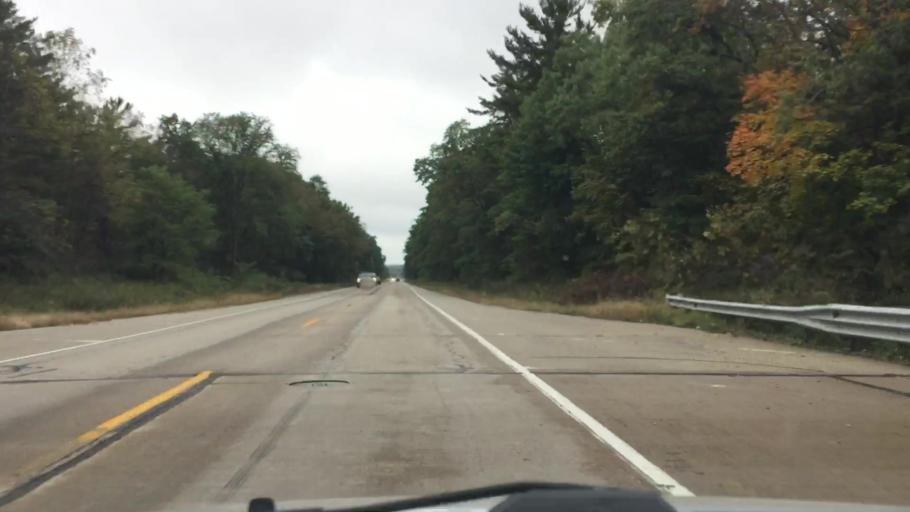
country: US
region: Wisconsin
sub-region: Rock County
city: Janesville
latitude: 42.7150
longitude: -89.0310
